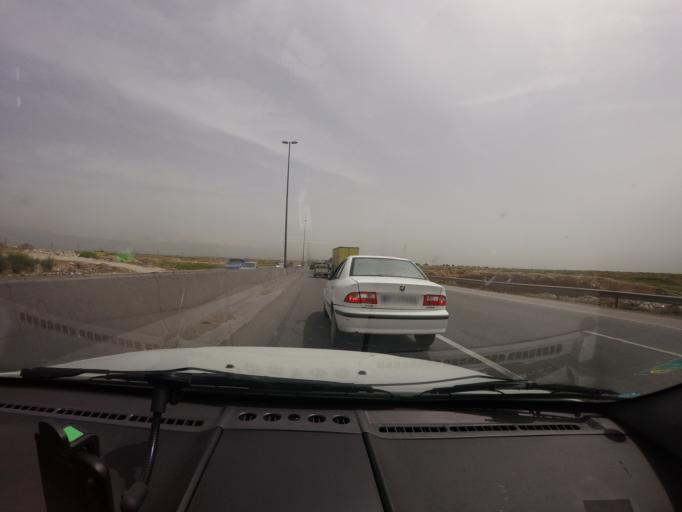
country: IR
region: Tehran
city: Eslamshahr
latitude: 35.5943
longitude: 51.1787
